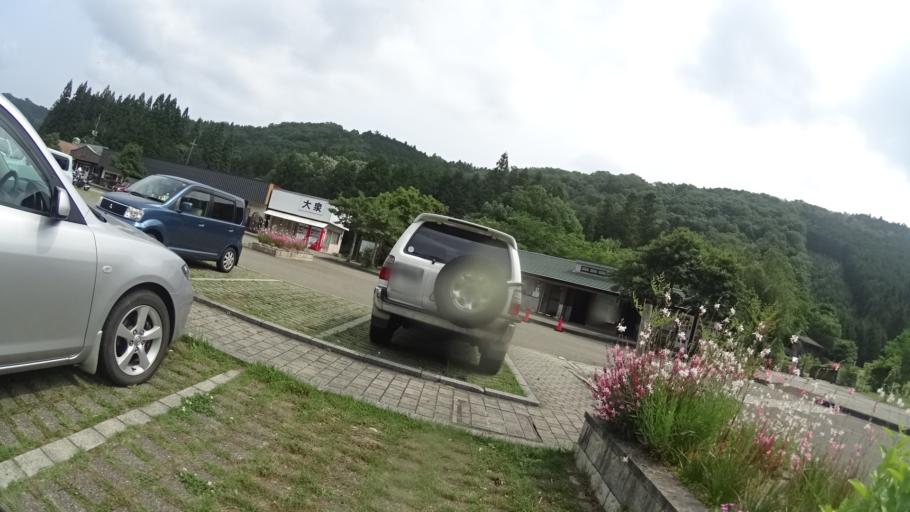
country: JP
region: Yamaguchi
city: Hagi
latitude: 34.2767
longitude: 131.3236
